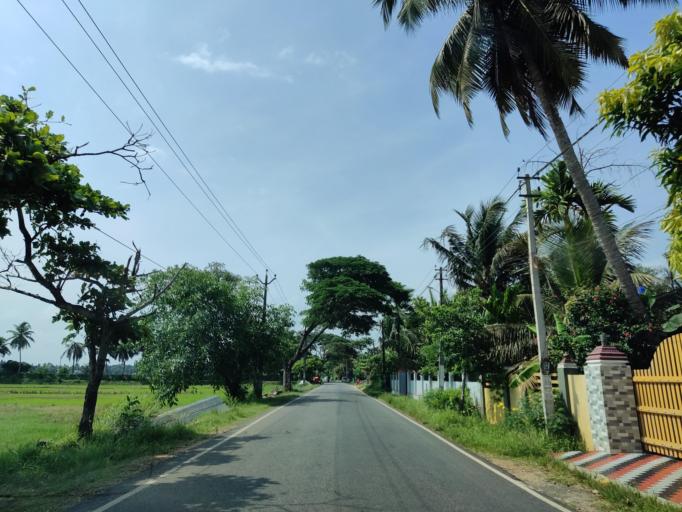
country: IN
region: Kerala
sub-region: Pattanamtitta
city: Tiruvalla
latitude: 9.3473
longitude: 76.4689
